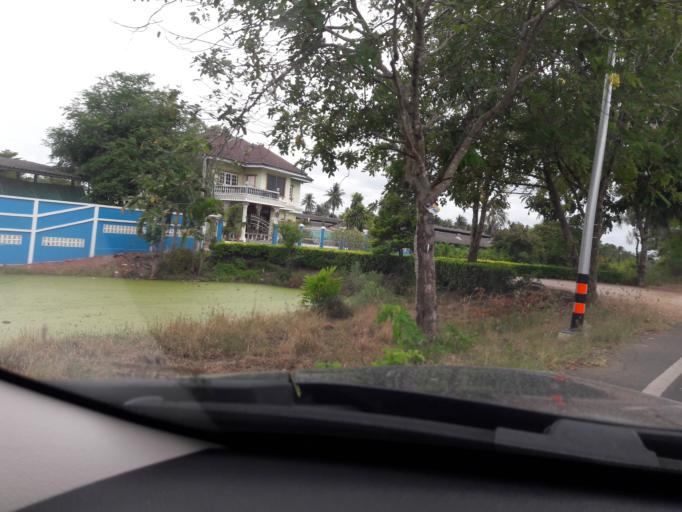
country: TH
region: Ratchaburi
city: Damnoen Saduak
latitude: 13.5947
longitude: 99.9450
